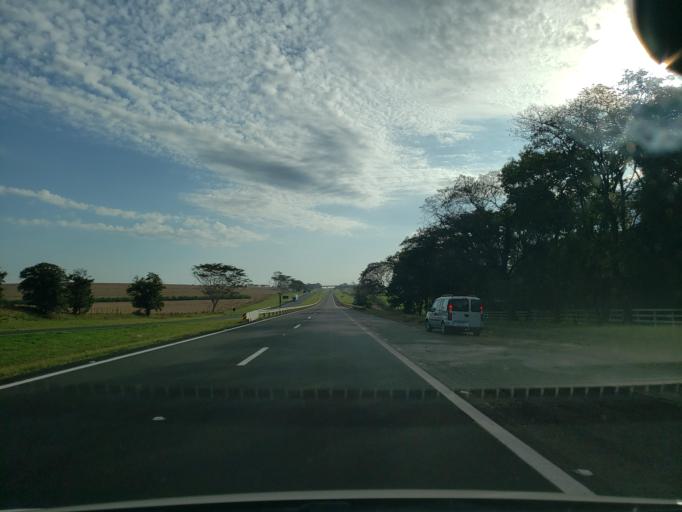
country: BR
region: Sao Paulo
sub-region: Valparaiso
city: Valparaiso
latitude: -21.2058
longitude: -50.7788
